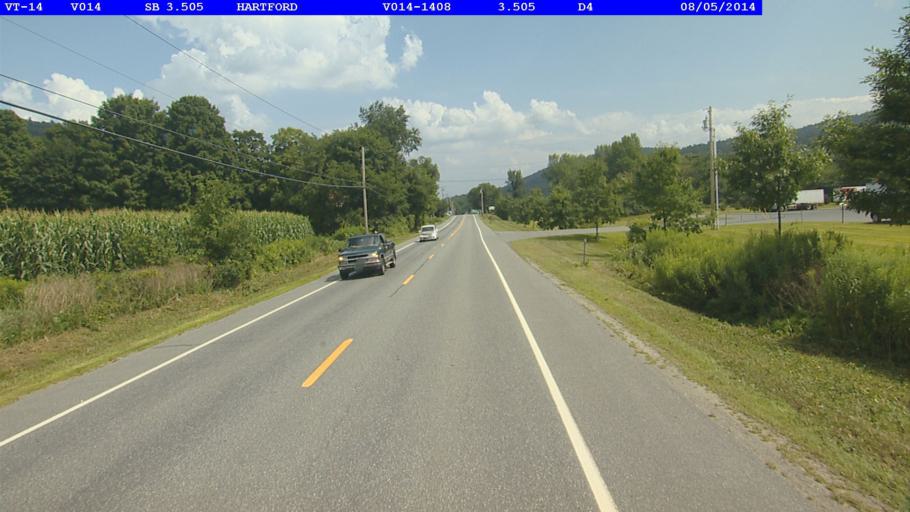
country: US
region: Vermont
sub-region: Windsor County
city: White River Junction
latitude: 43.6734
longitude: -72.3811
